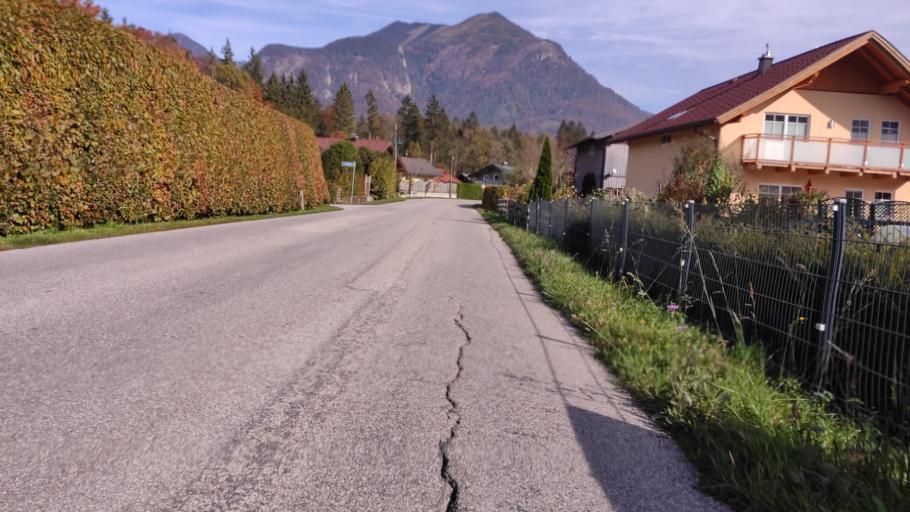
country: AT
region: Salzburg
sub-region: Politischer Bezirk Salzburg-Umgebung
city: Strobl
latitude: 47.7171
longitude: 13.5160
